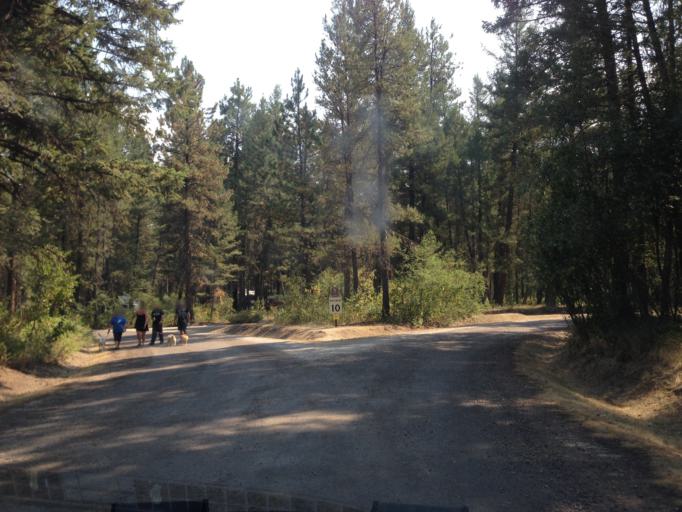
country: CA
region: British Columbia
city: Cranbrook
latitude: 49.5387
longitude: -115.4861
